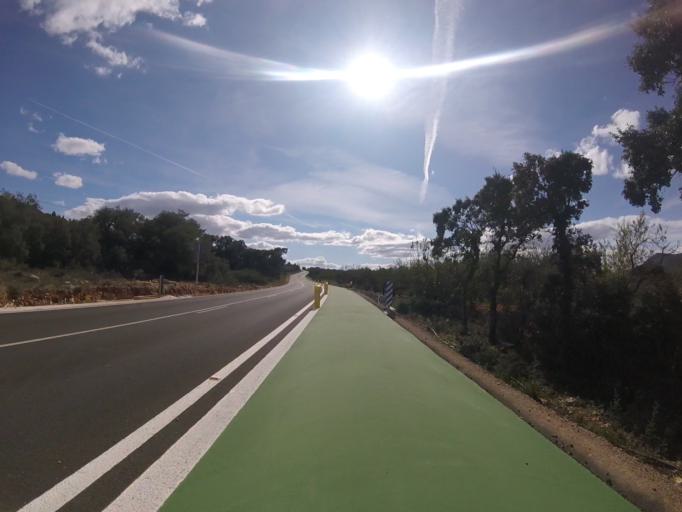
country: ES
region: Valencia
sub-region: Provincia de Castello
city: Cati
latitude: 40.4152
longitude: 0.0711
